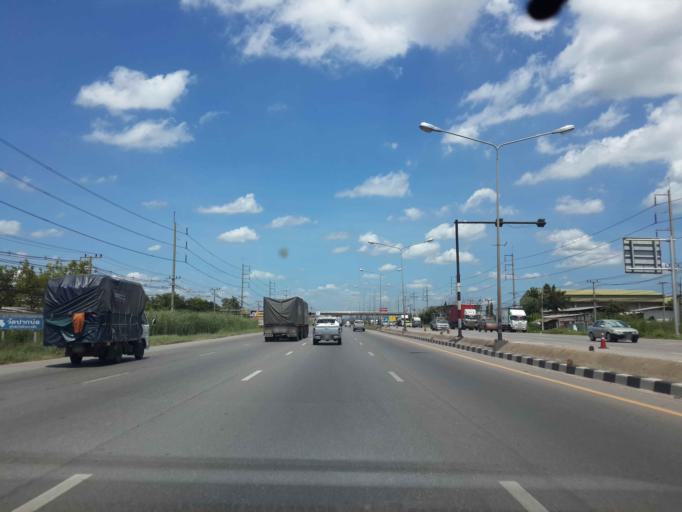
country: TH
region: Samut Sakhon
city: Samut Sakhon
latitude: 13.5277
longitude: 100.1939
